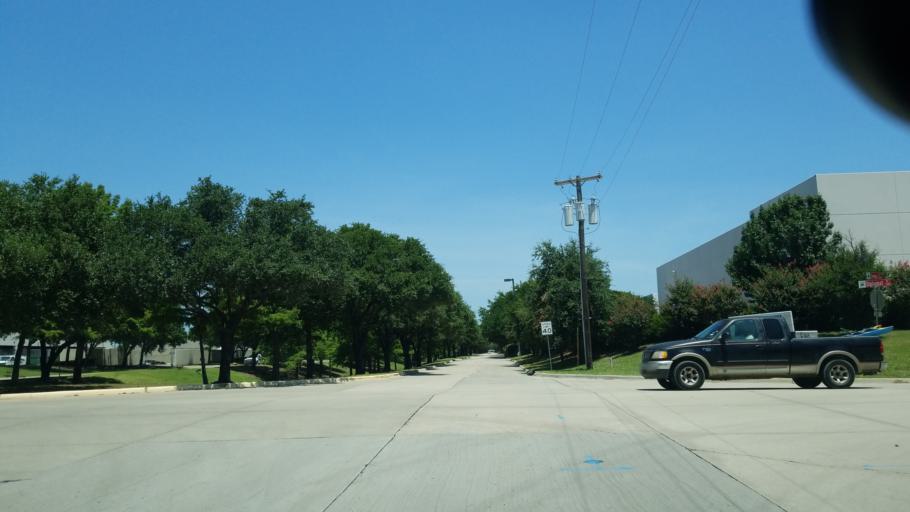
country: US
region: Texas
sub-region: Dallas County
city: Farmers Branch
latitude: 32.9283
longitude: -96.9093
